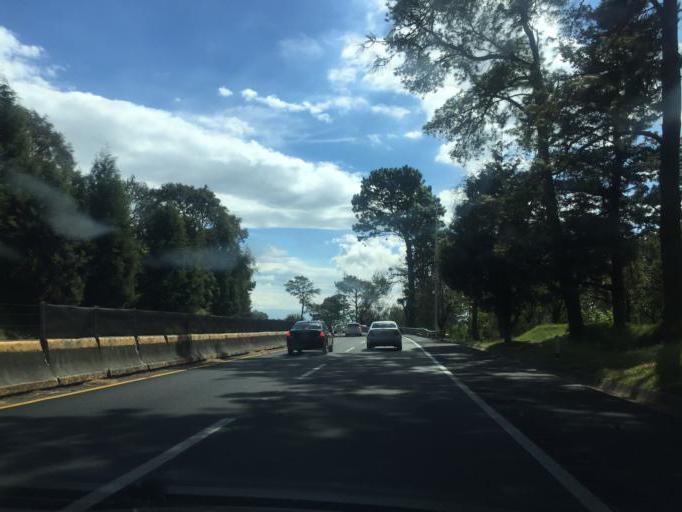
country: MX
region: Morelos
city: Tres Marias
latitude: 19.0312
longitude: -99.2209
